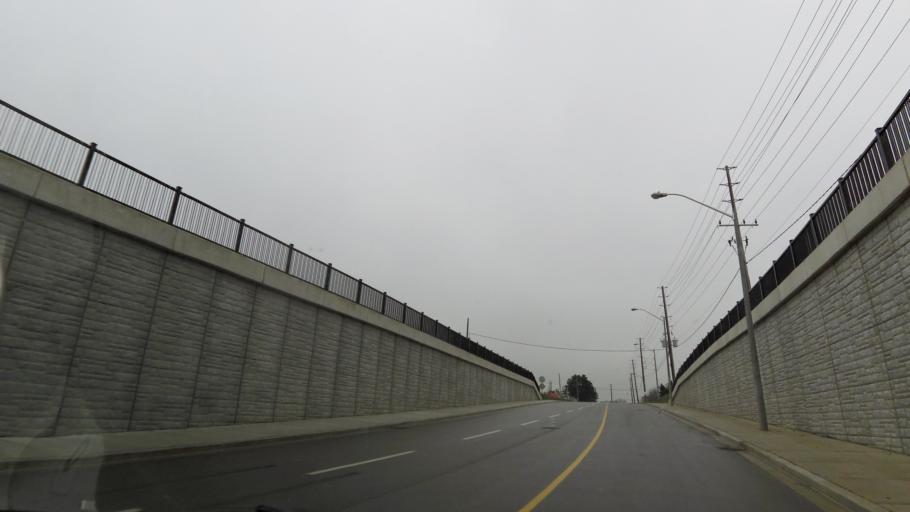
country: CA
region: Ontario
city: Etobicoke
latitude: 43.7054
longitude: -79.6039
